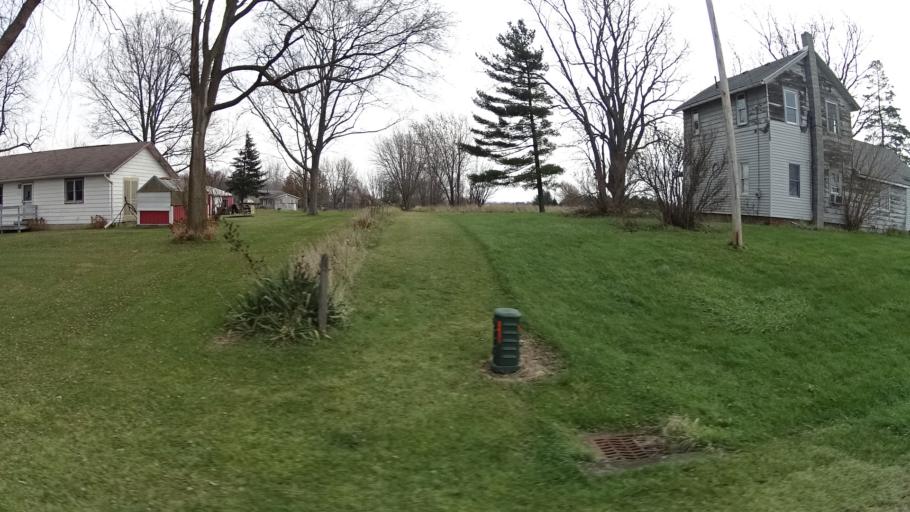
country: US
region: Ohio
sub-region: Lorain County
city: Wellington
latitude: 41.1408
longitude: -82.1698
